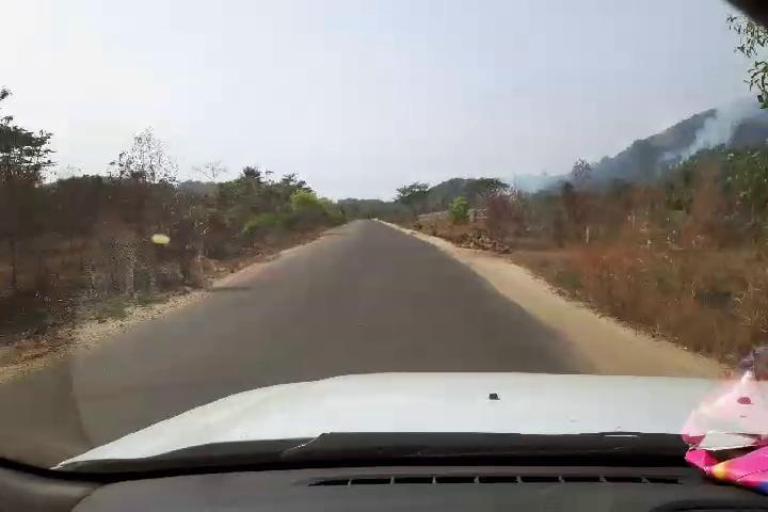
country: SL
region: Western Area
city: Waterloo
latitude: 8.2530
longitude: -13.1553
